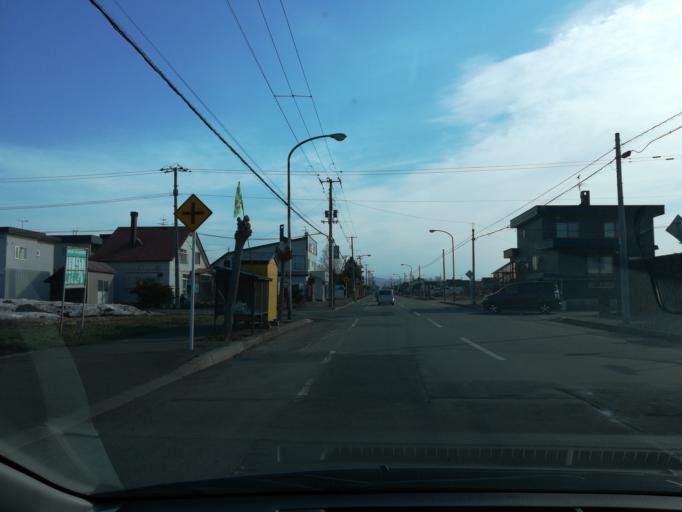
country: JP
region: Hokkaido
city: Iwamizawa
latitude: 43.2017
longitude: 141.7455
